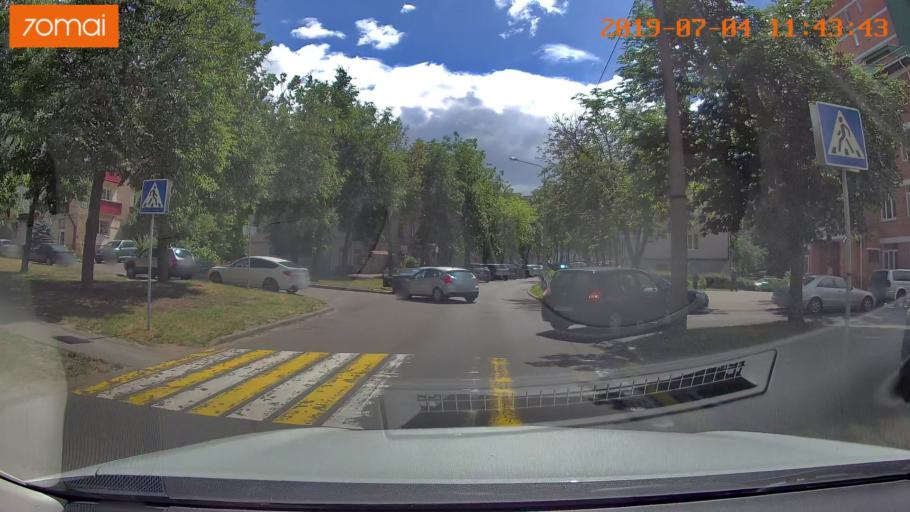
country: BY
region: Minsk
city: Minsk
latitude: 53.9269
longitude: 27.6009
